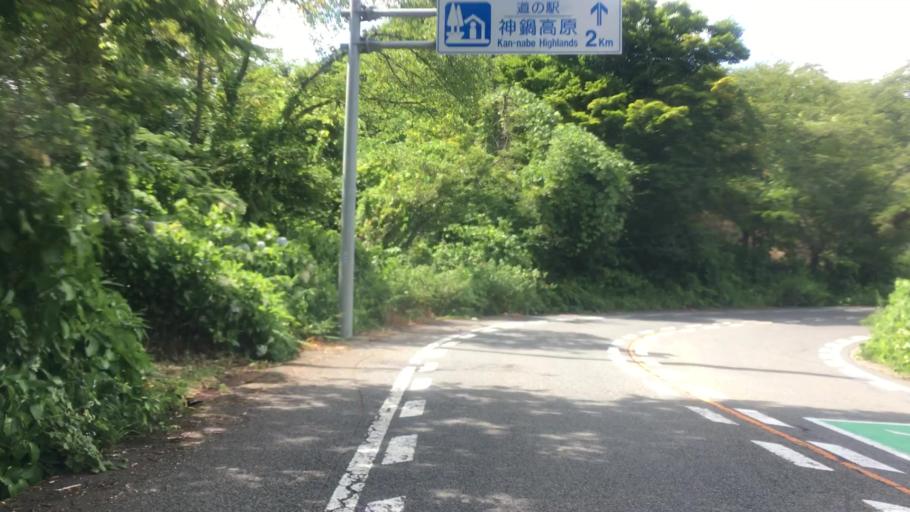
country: JP
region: Hyogo
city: Toyooka
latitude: 35.4904
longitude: 134.6883
